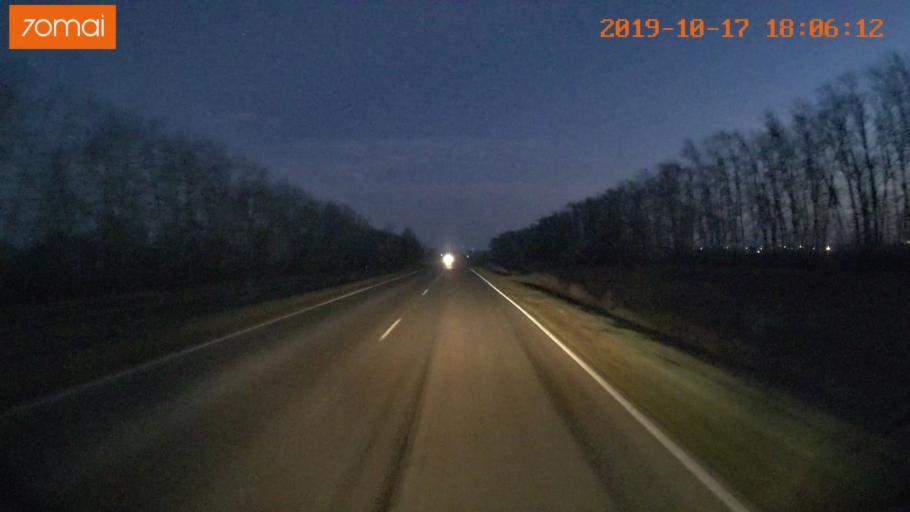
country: RU
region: Tula
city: Kurkino
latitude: 53.4551
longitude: 38.6529
